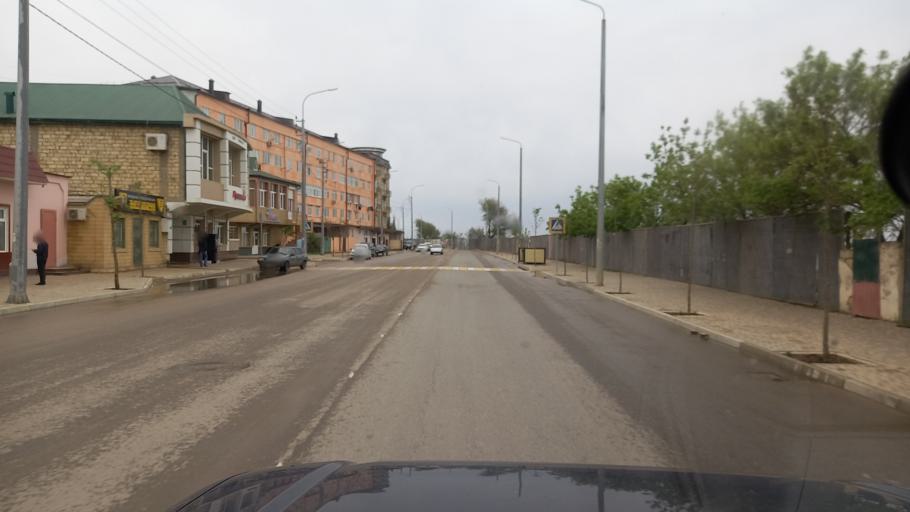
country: RU
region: Dagestan
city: Derbent
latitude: 42.0842
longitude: 48.2935
